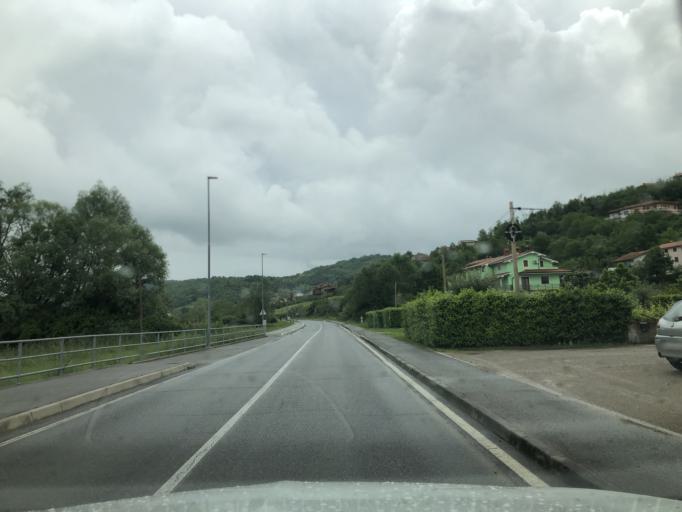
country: SI
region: Koper-Capodistria
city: Prade
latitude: 45.5190
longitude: 13.7558
